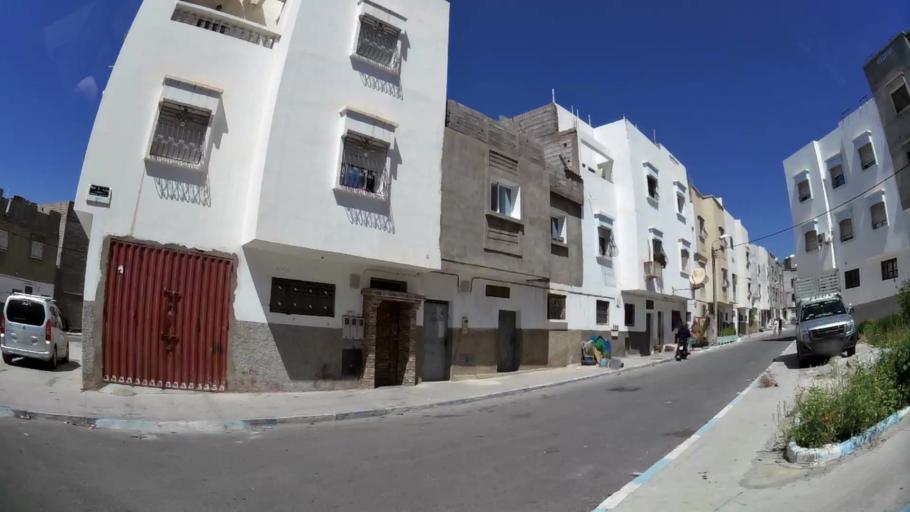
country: MA
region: Oued ed Dahab-Lagouira
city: Dakhla
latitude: 30.4399
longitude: -9.5535
